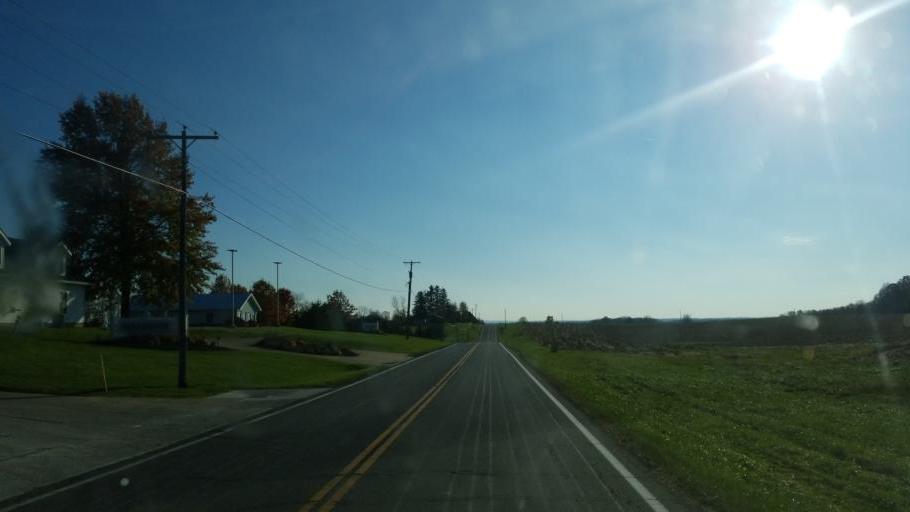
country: US
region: Ohio
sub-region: Sandusky County
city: Bellville
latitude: 40.5567
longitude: -82.5364
